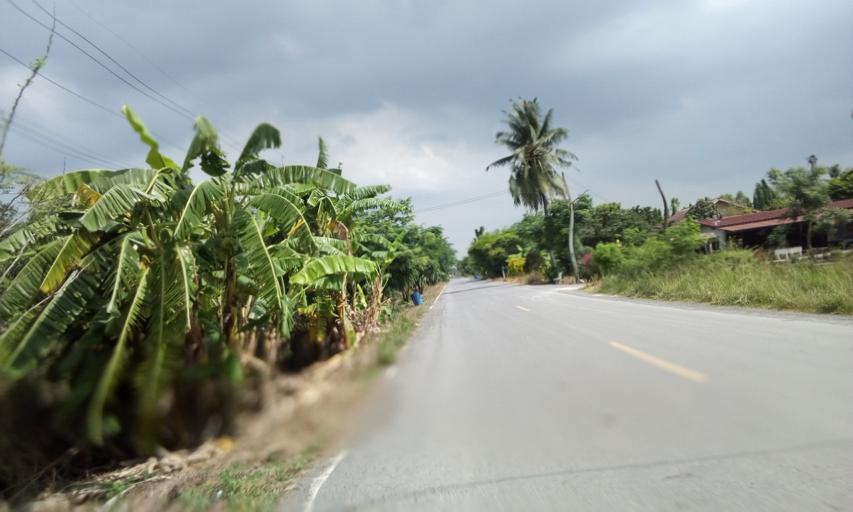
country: TH
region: Pathum Thani
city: Ban Lam Luk Ka
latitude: 14.0325
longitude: 100.8474
